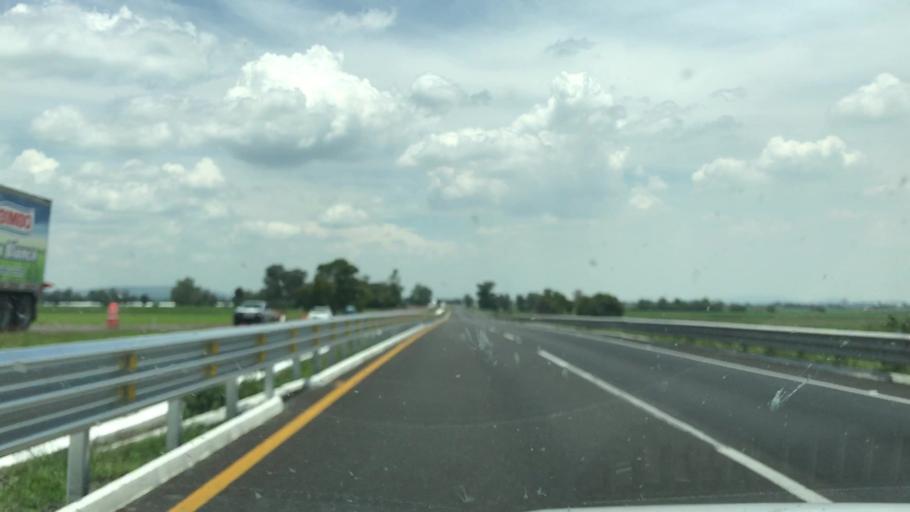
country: MX
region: Guanajuato
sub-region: Irapuato
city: Cuarta Brigada
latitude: 20.6446
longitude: -101.2727
